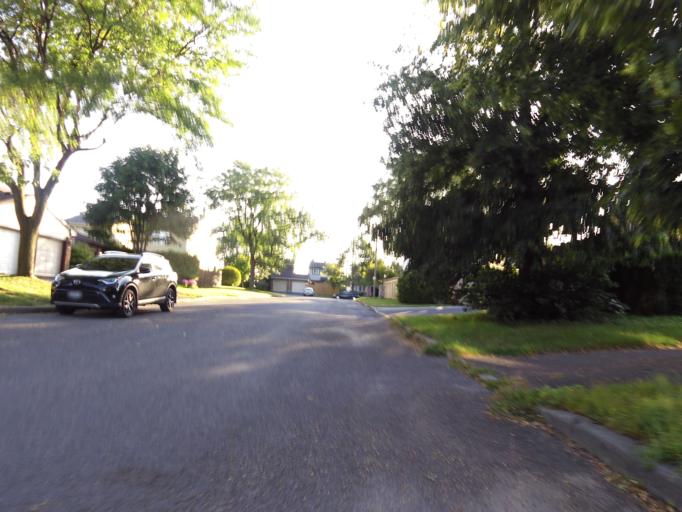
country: CA
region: Ontario
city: Ottawa
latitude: 45.3709
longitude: -75.7142
